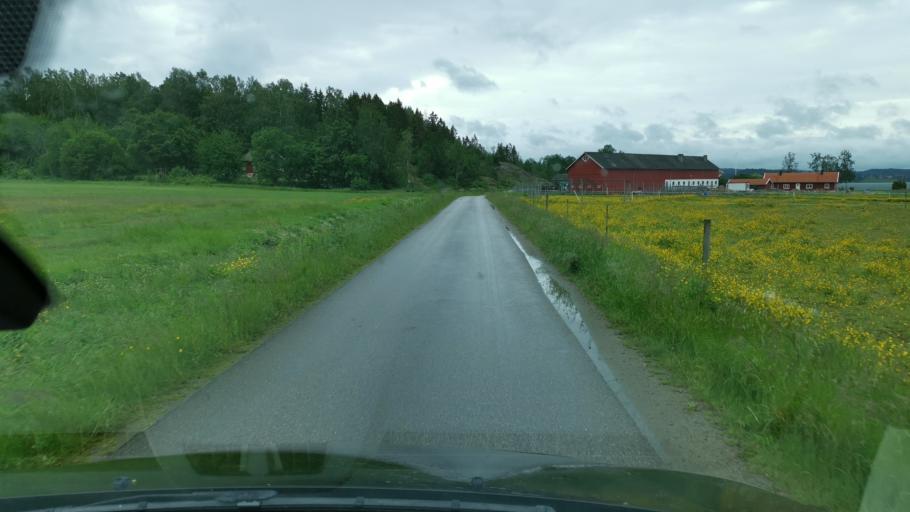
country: SE
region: Vaestra Goetaland
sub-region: Orust
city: Henan
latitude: 58.3227
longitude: 11.7178
